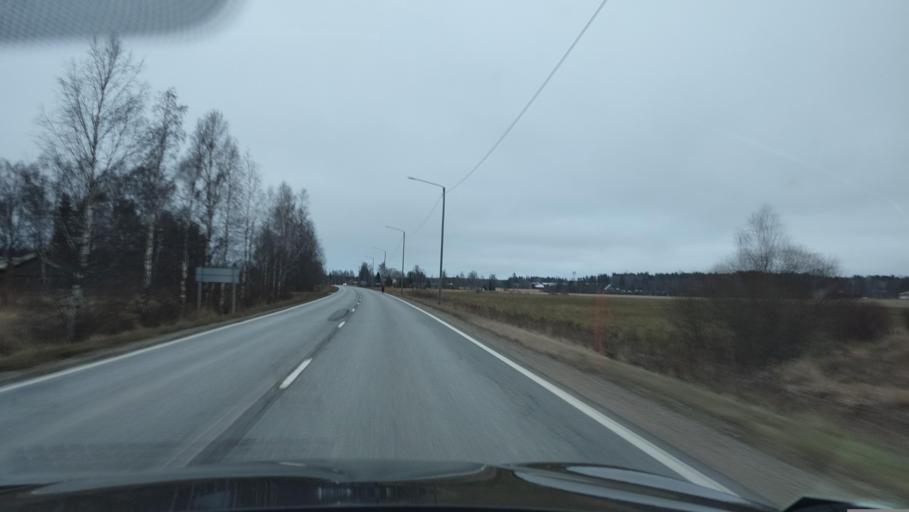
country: FI
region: Southern Ostrobothnia
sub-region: Suupohja
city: Kauhajoki
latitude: 62.3514
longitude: 22.0529
